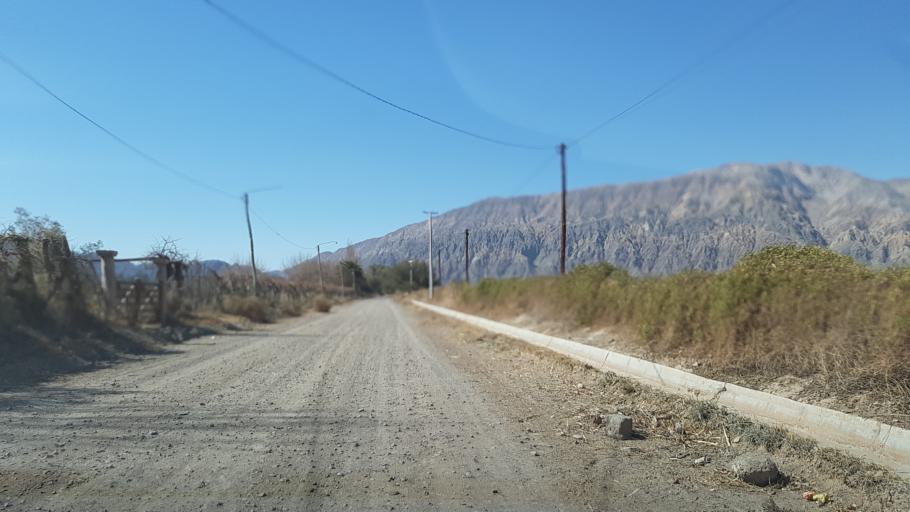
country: AR
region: San Juan
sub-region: Departamento de Zonda
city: Zonda
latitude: -31.5711
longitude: -68.7486
